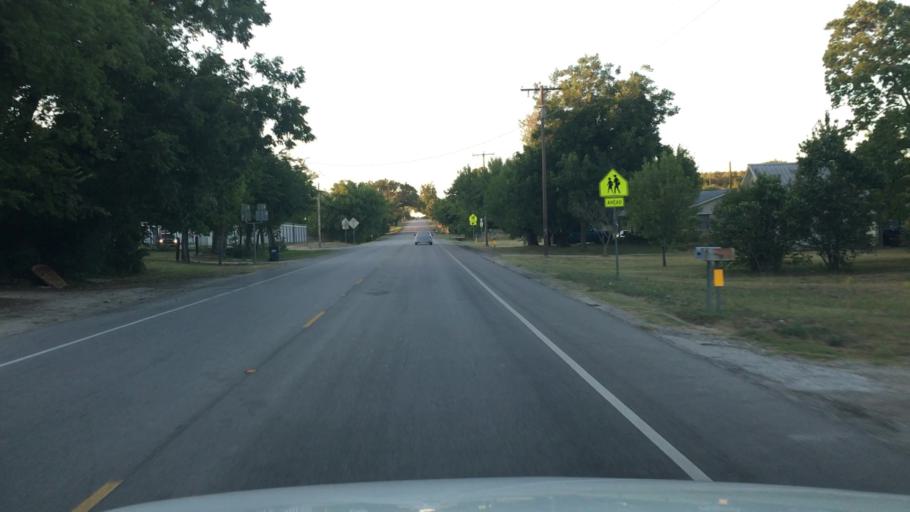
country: US
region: Texas
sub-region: Hamilton County
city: Hico
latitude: 31.9852
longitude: -98.0277
